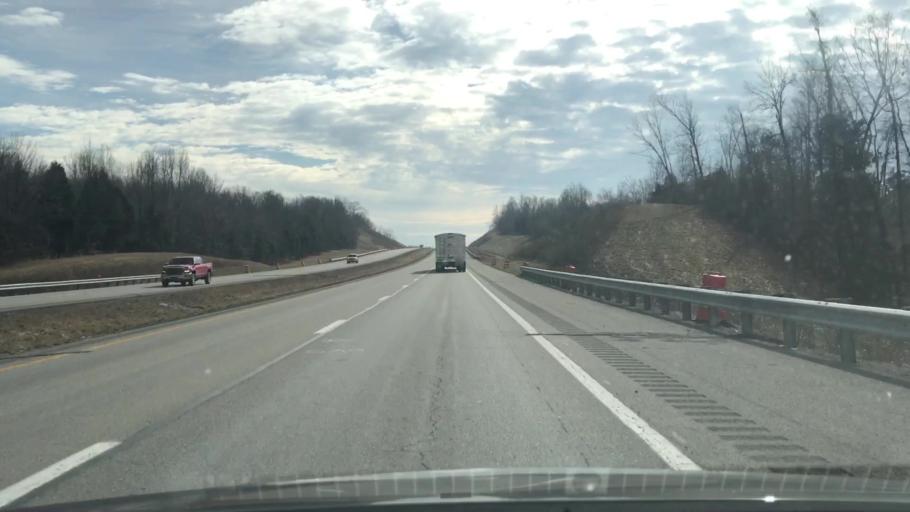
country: US
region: Kentucky
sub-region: Ohio County
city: Hartford
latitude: 37.5731
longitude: -86.9520
